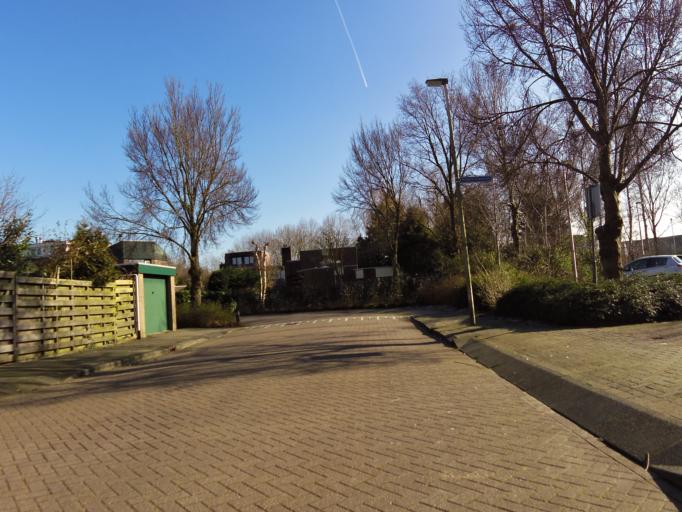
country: NL
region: South Holland
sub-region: Gemeente Leiderdorp
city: Leiderdorp
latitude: 52.1599
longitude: 4.5440
